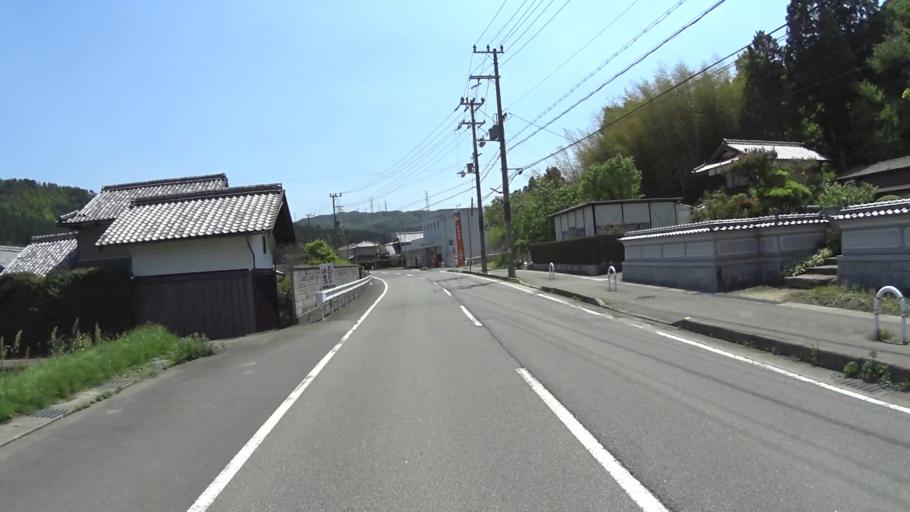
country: JP
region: Kyoto
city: Kameoka
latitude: 35.0171
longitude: 135.4872
